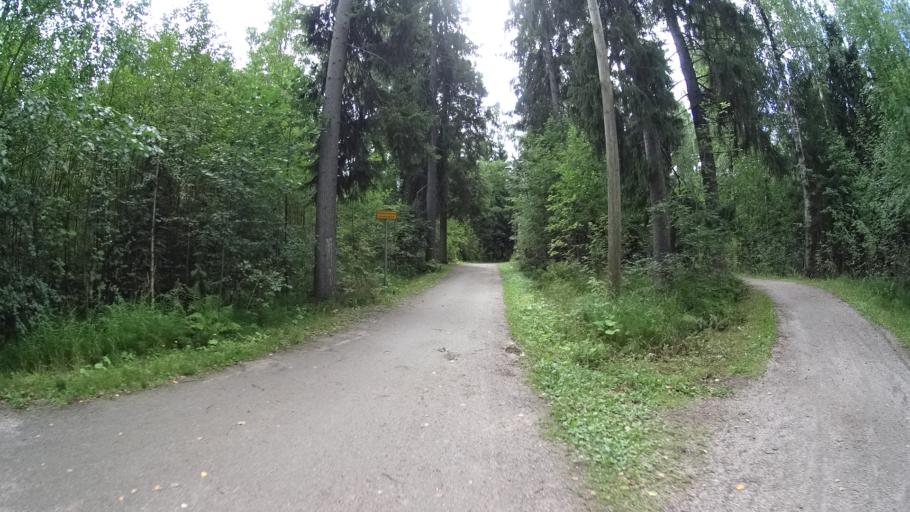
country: FI
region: Uusimaa
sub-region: Helsinki
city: Helsinki
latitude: 60.2622
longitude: 24.9028
